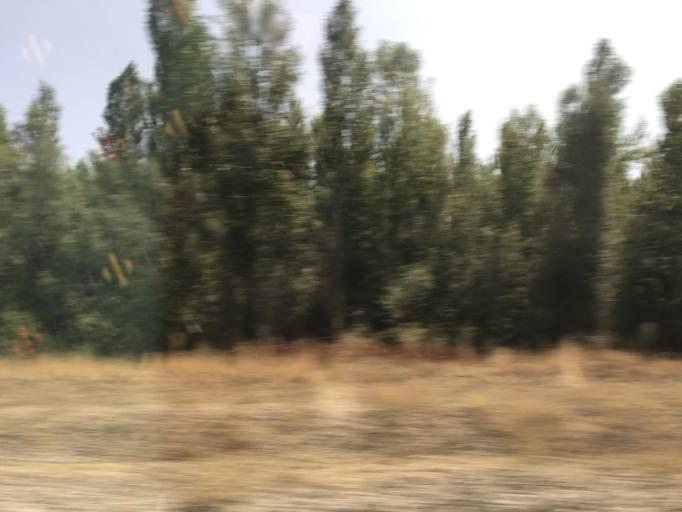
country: ES
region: Castille and Leon
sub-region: Provincia de Palencia
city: Soto de Cerrato
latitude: 41.9602
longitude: -4.4437
